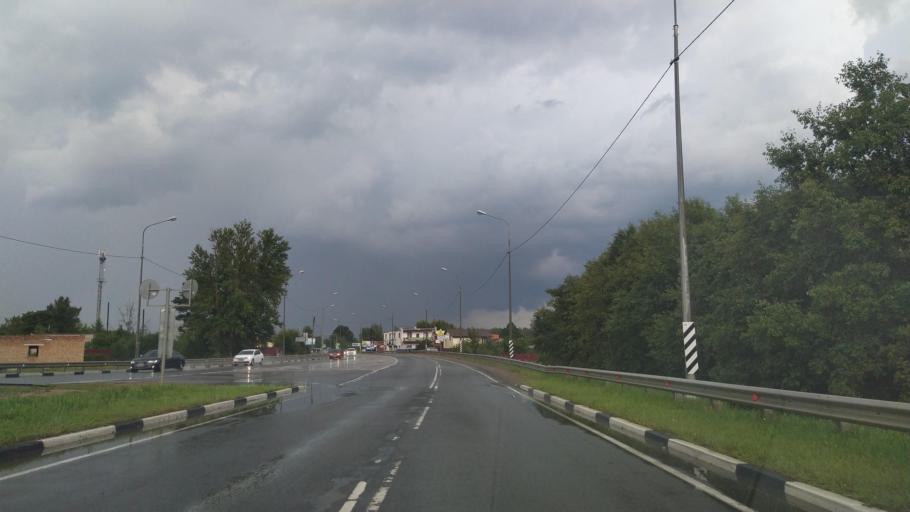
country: RU
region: Pskov
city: Pskov
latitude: 57.7424
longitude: 28.3687
